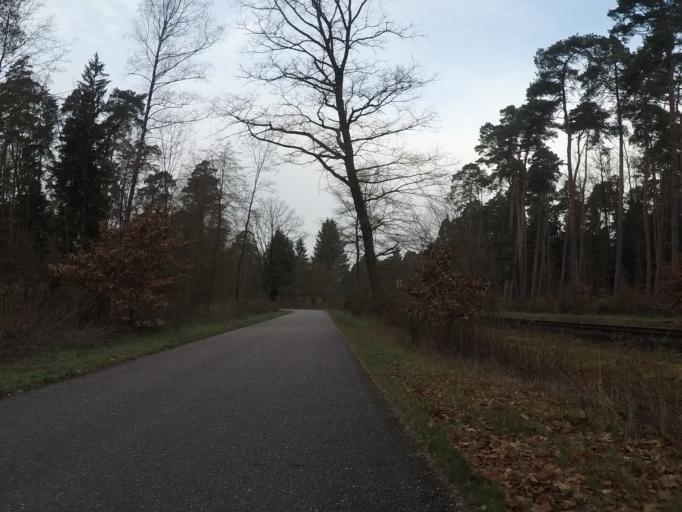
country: DE
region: Rheinland-Pfalz
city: Kandel
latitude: 49.0681
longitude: 8.2253
